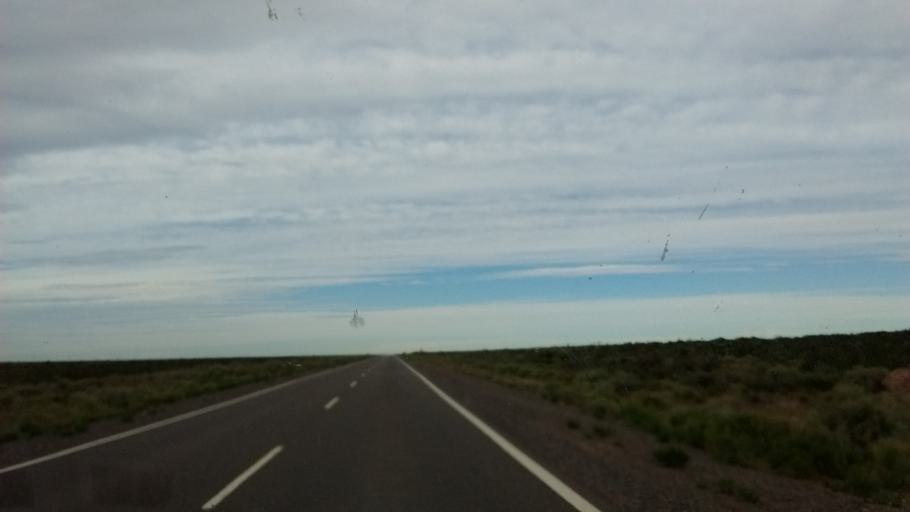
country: AR
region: Rio Negro
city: Contraalmirante Cordero
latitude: -38.4690
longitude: -68.0493
